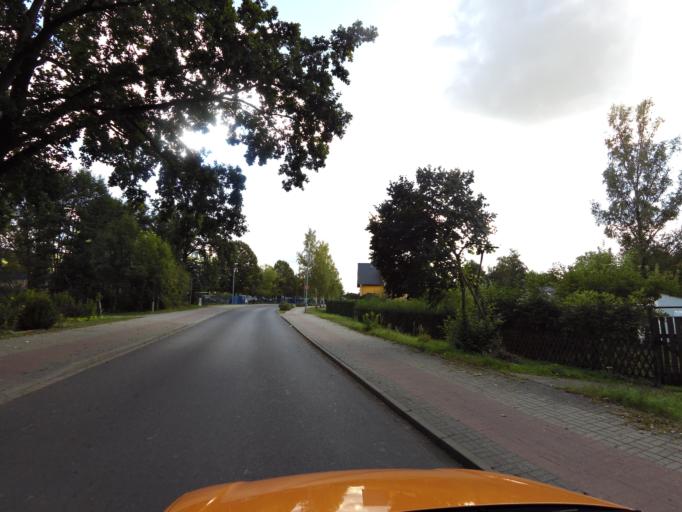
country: DE
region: Brandenburg
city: Luckenwalde
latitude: 52.0813
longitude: 13.1692
